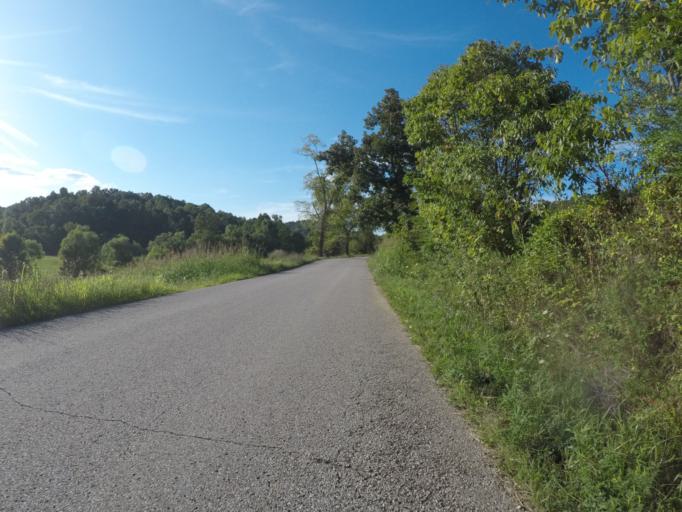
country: US
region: West Virginia
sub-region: Cabell County
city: Huntington
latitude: 38.5162
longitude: -82.5006
